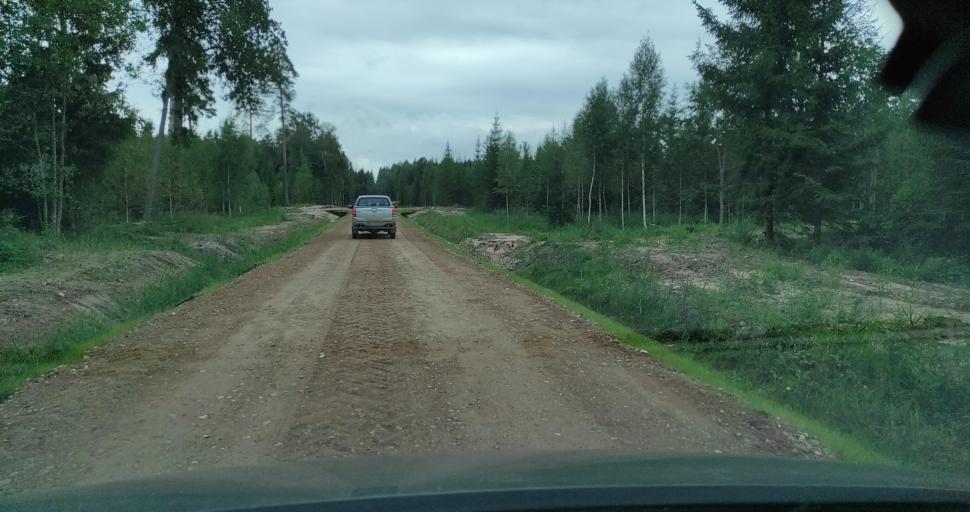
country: LV
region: Talsu Rajons
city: Sabile
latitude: 57.0176
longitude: 22.3538
